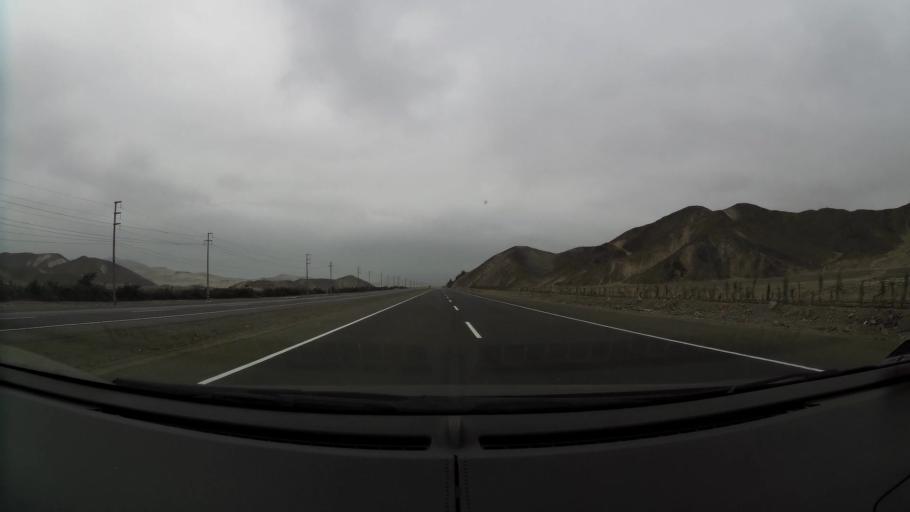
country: PE
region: La Libertad
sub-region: Viru
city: Chao
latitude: -8.6164
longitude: -78.6560
